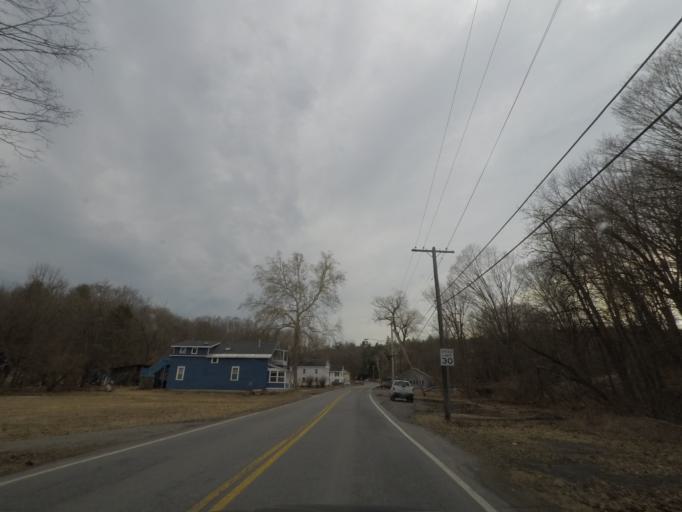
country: US
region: New York
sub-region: Washington County
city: Greenwich
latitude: 43.0827
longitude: -73.4949
